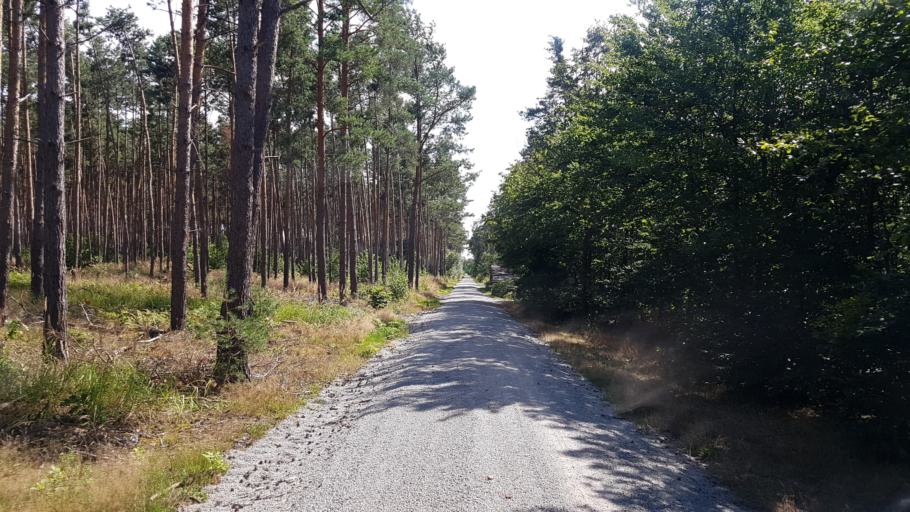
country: DE
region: Brandenburg
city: Bad Liebenwerda
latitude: 51.4791
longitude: 13.3120
